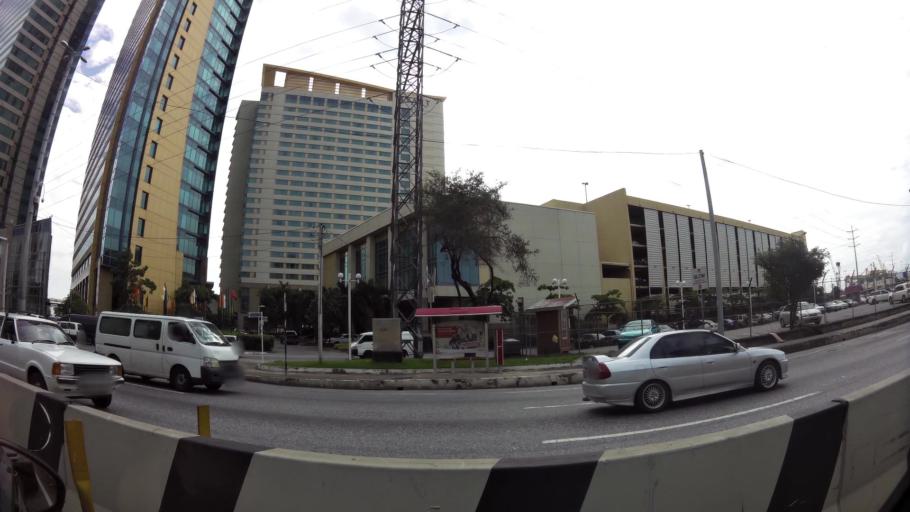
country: TT
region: City of Port of Spain
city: Port-of-Spain
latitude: 10.6513
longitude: -61.5154
